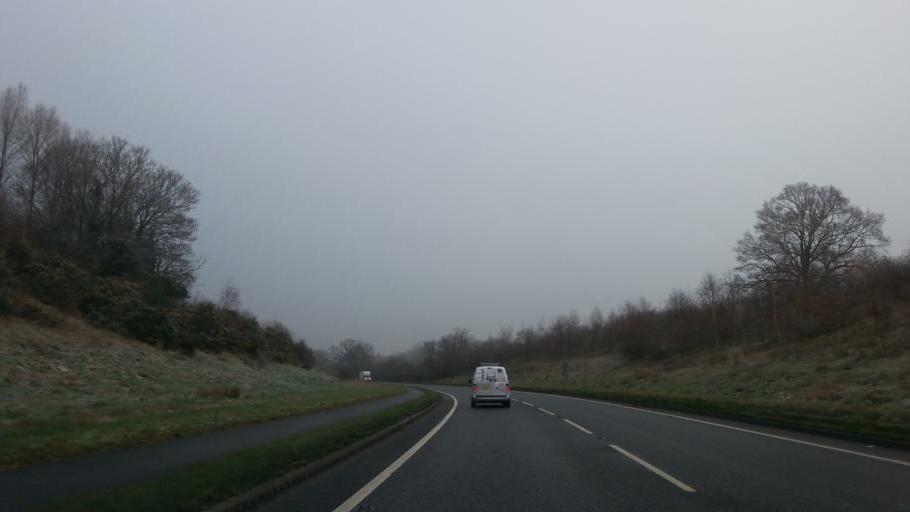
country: GB
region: England
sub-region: Cheshire East
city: Alderley Edge
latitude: 53.3090
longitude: -2.2413
